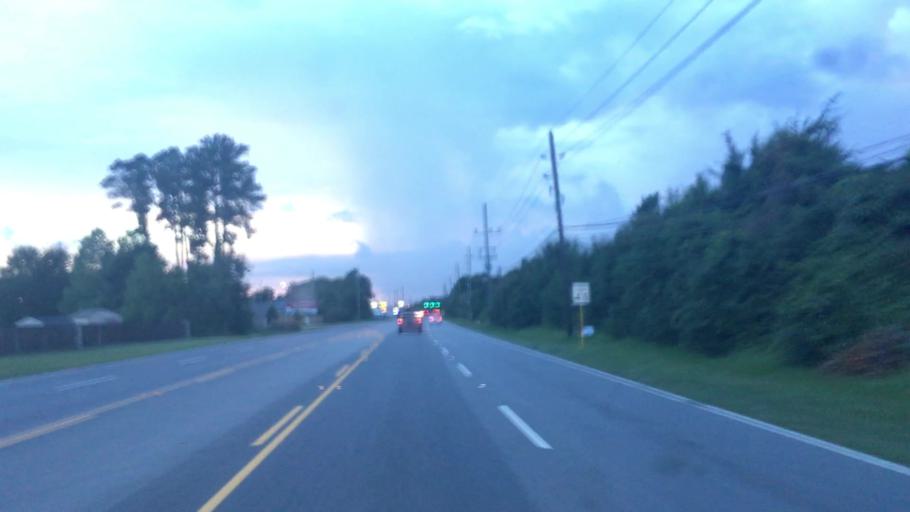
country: US
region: Texas
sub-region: Harris County
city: Humble
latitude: 29.9768
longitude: -95.2224
